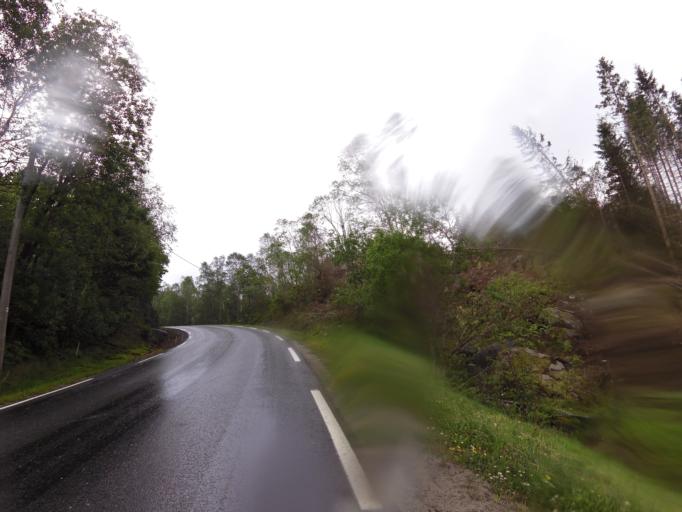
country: NO
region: Vest-Agder
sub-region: Lyngdal
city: Lyngdal
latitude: 58.1116
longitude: 7.0842
